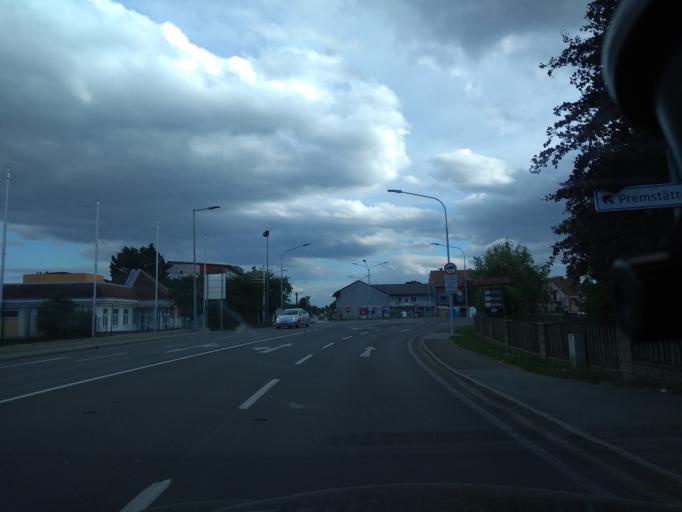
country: AT
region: Styria
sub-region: Politischer Bezirk Graz-Umgebung
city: Seiersberg
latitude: 47.0097
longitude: 15.3990
